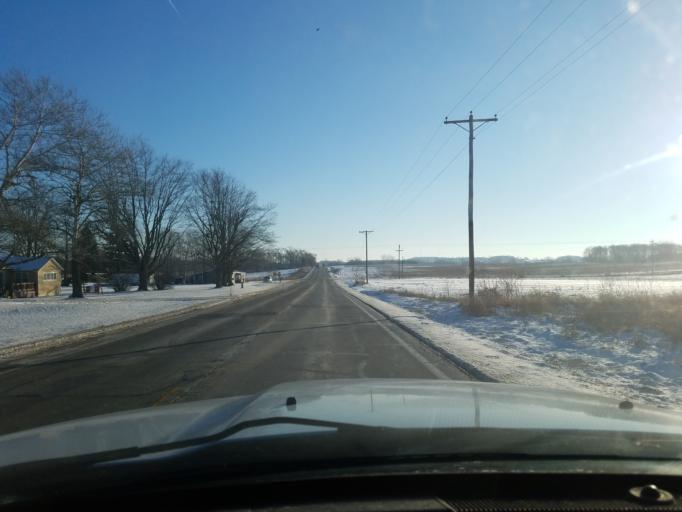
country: US
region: Indiana
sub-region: Noble County
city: Ligonier
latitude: 41.4523
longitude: -85.5692
